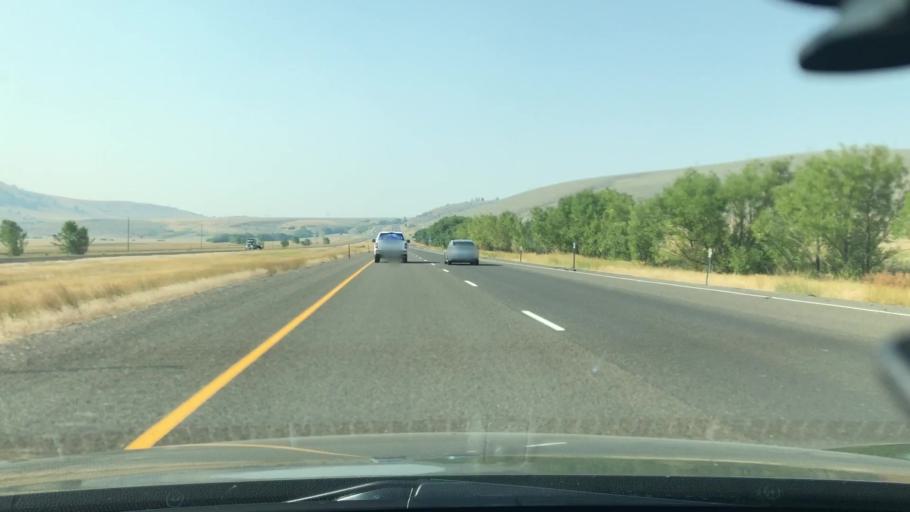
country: US
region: Oregon
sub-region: Union County
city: Union
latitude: 45.1288
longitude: -117.9642
